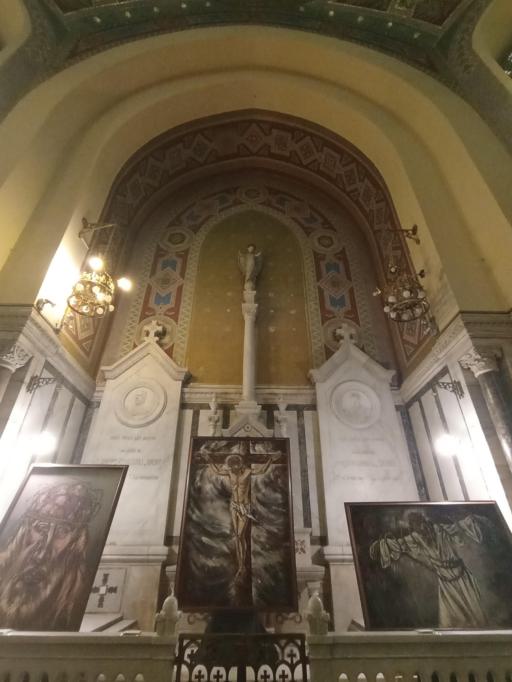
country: ES
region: Madrid
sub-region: Provincia de Madrid
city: Retiro
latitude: 40.4210
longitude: -3.6865
